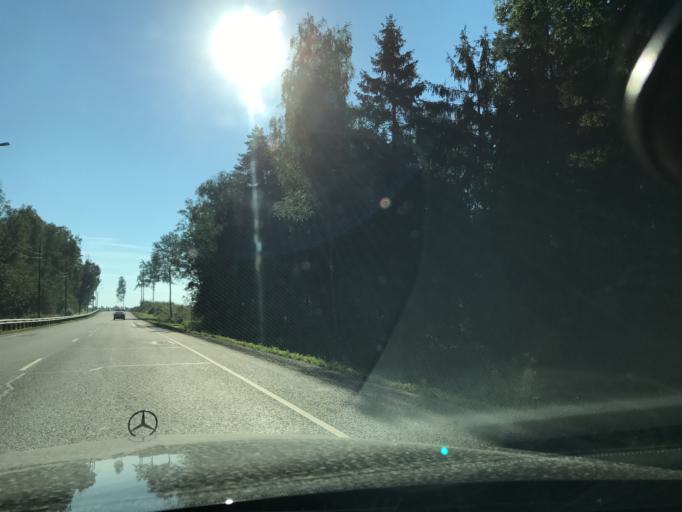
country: RU
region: Moskovskaya
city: Sverdlovskiy
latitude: 55.9279
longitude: 38.1921
